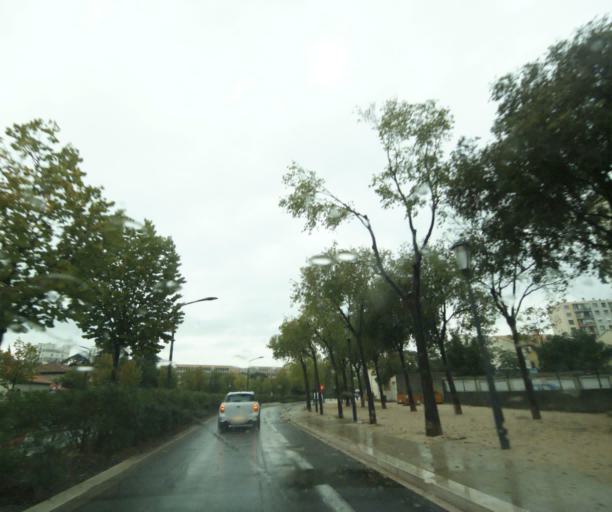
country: FR
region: Languedoc-Roussillon
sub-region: Departement du Gard
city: Nimes
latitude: 43.8232
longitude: 4.3549
